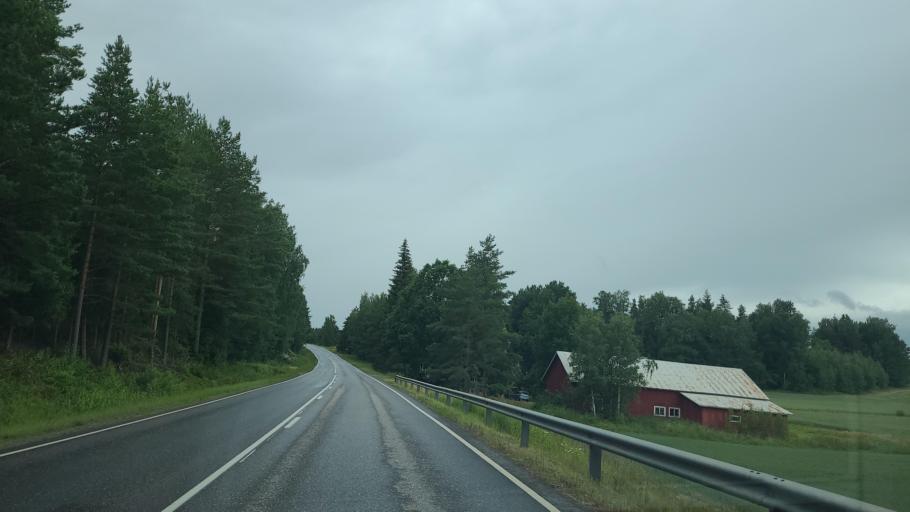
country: FI
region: Varsinais-Suomi
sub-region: Turku
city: Sauvo
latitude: 60.3142
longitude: 22.6928
